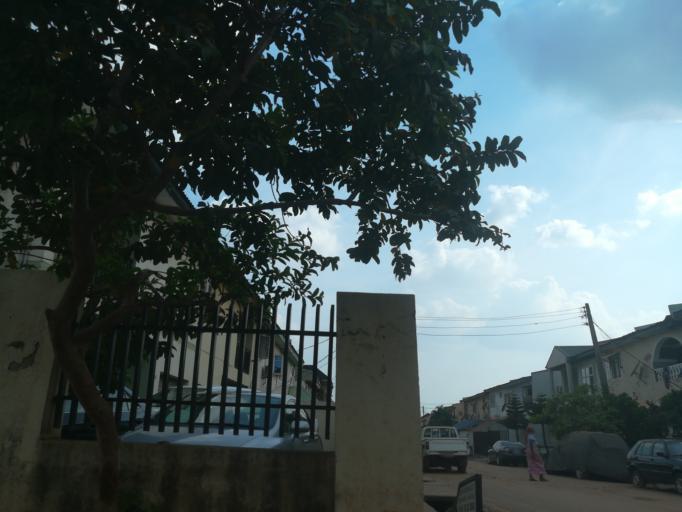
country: NG
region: Abuja Federal Capital Territory
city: Abuja
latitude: 9.0829
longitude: 7.4136
